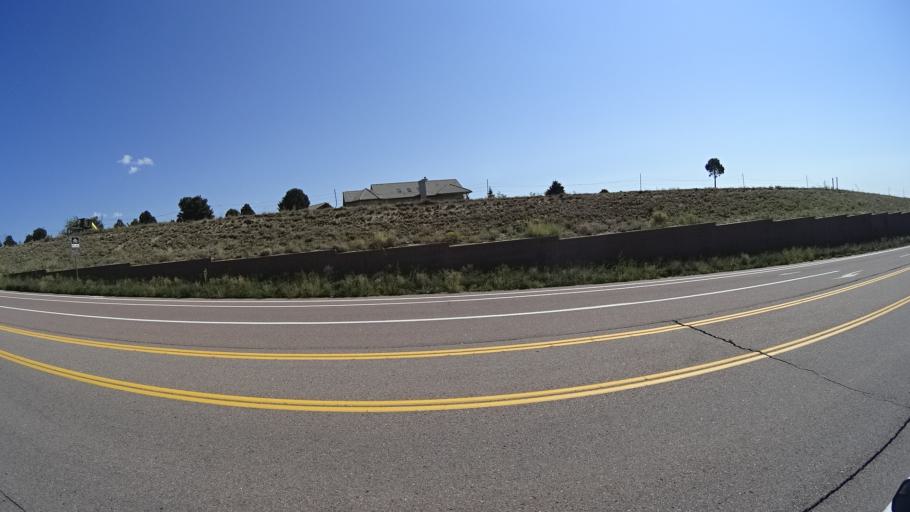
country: US
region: Colorado
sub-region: El Paso County
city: Cimarron Hills
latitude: 38.9321
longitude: -104.7015
